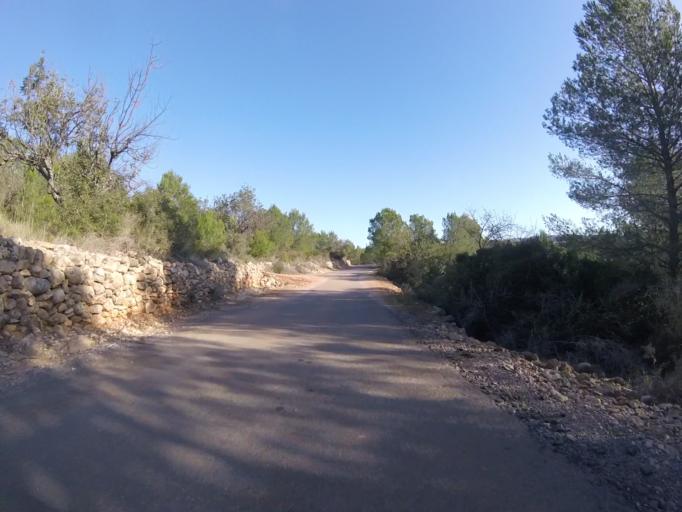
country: ES
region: Valencia
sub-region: Provincia de Castello
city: Alcala de Xivert
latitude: 40.2749
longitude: 0.2083
